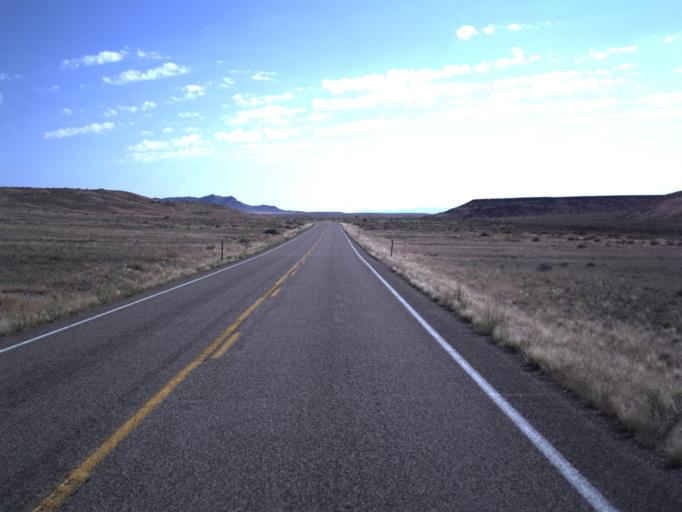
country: US
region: Utah
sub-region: Beaver County
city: Milford
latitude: 38.7434
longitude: -112.9557
